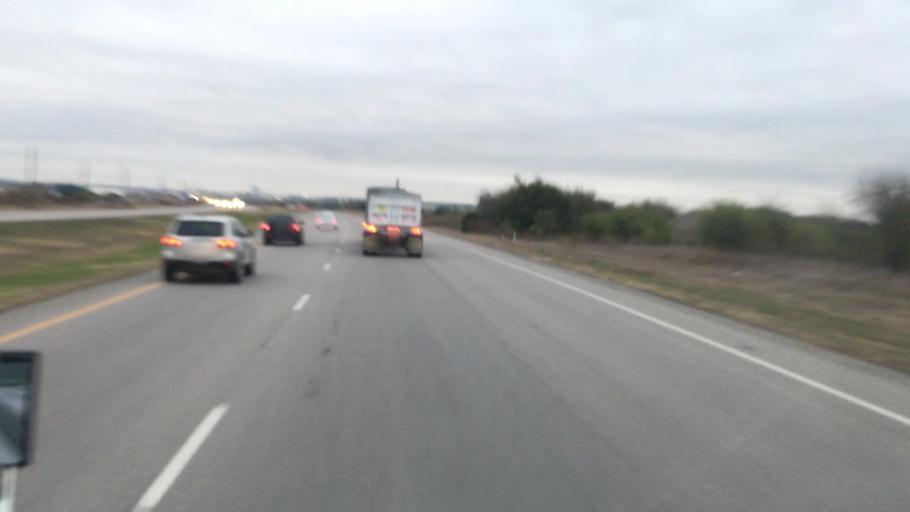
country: US
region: Texas
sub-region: Johnson County
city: Venus
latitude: 32.4361
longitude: -97.1020
